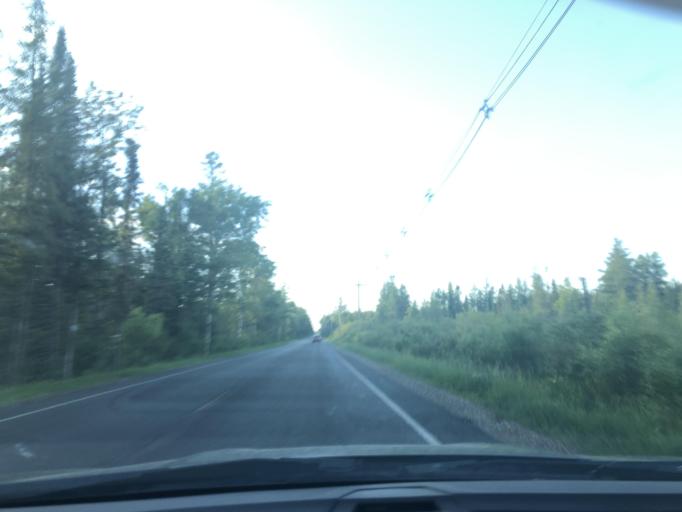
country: US
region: Michigan
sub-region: Missaukee County
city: Lake City
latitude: 44.3689
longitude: -85.0760
